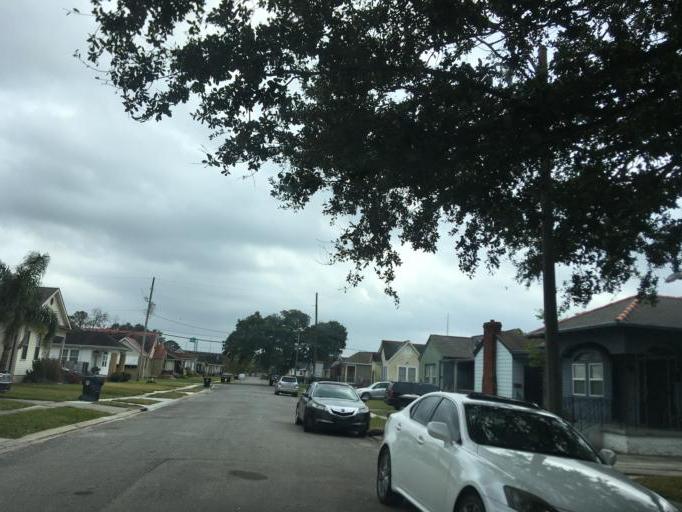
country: US
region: Louisiana
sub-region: Orleans Parish
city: New Orleans
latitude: 29.9945
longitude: -90.0528
